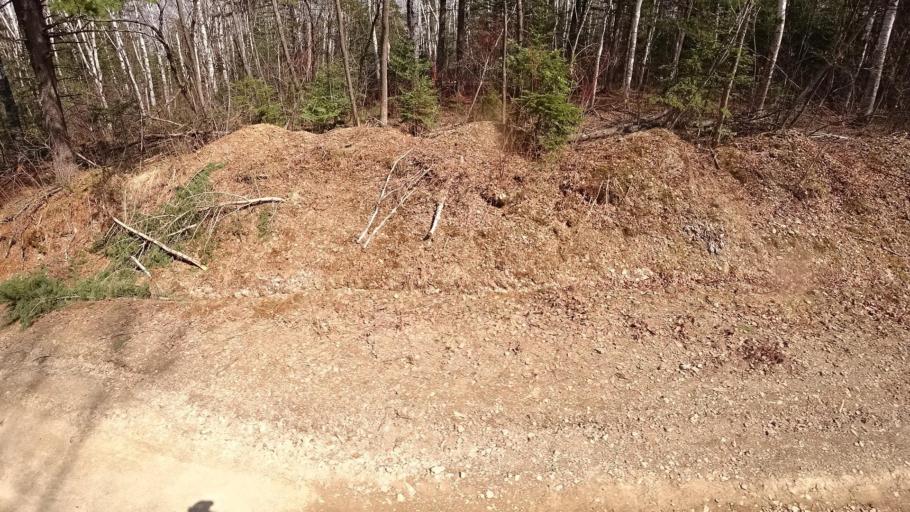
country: RU
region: Khabarovsk Krai
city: Selikhino
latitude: 50.6611
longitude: 137.4037
